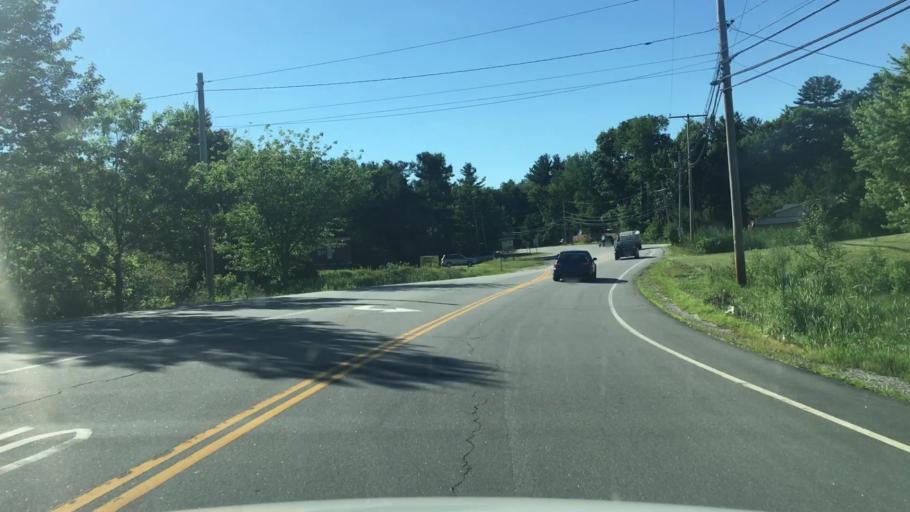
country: US
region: New Hampshire
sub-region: Rockingham County
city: Exeter
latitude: 43.0125
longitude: -71.0070
